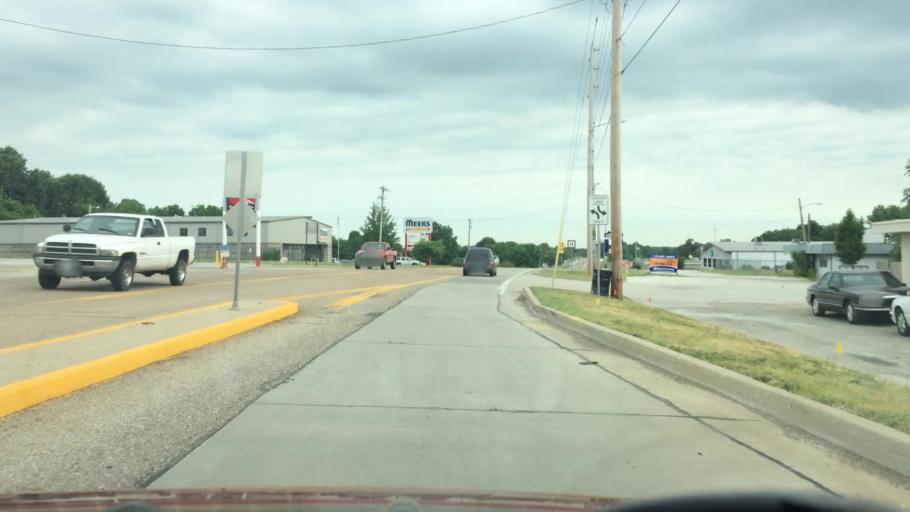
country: US
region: Missouri
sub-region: Greene County
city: Springfield
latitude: 37.2545
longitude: -93.2649
